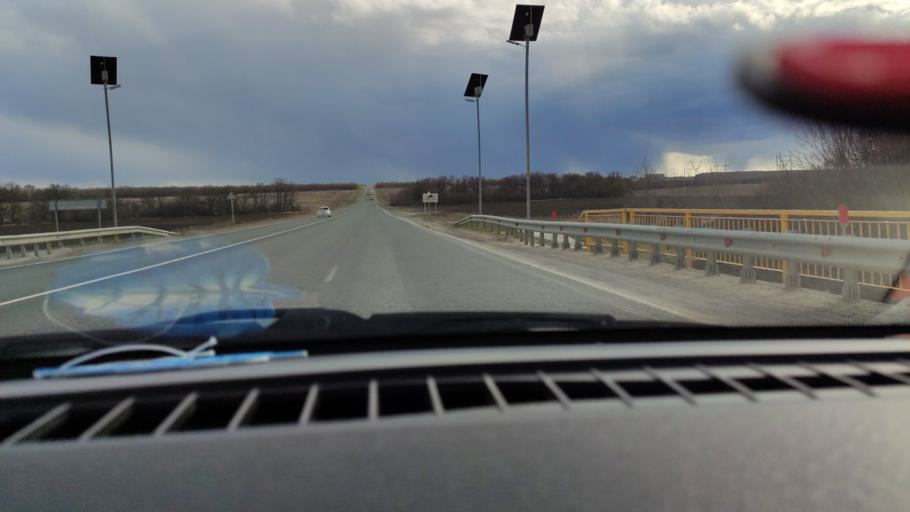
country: RU
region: Saratov
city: Sinodskoye
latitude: 51.9168
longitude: 46.5578
